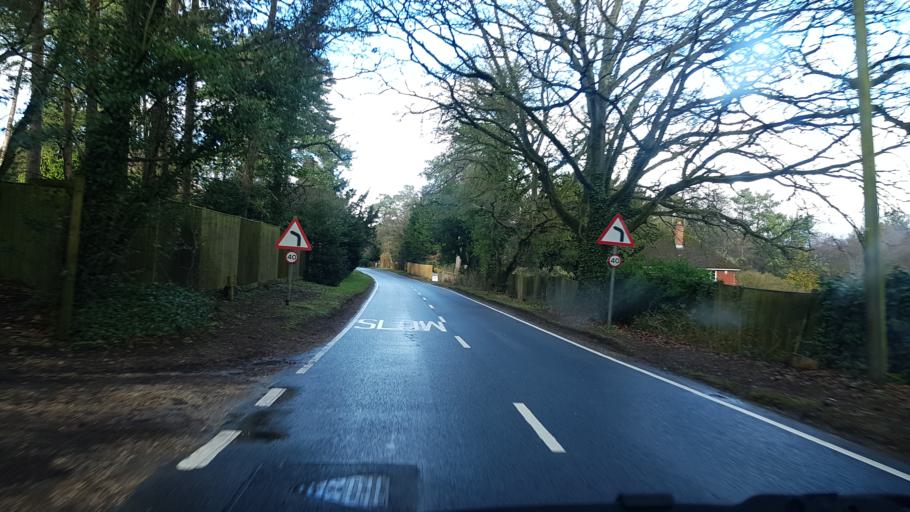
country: GB
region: England
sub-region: Surrey
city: Elstead
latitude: 51.1748
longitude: -0.7485
